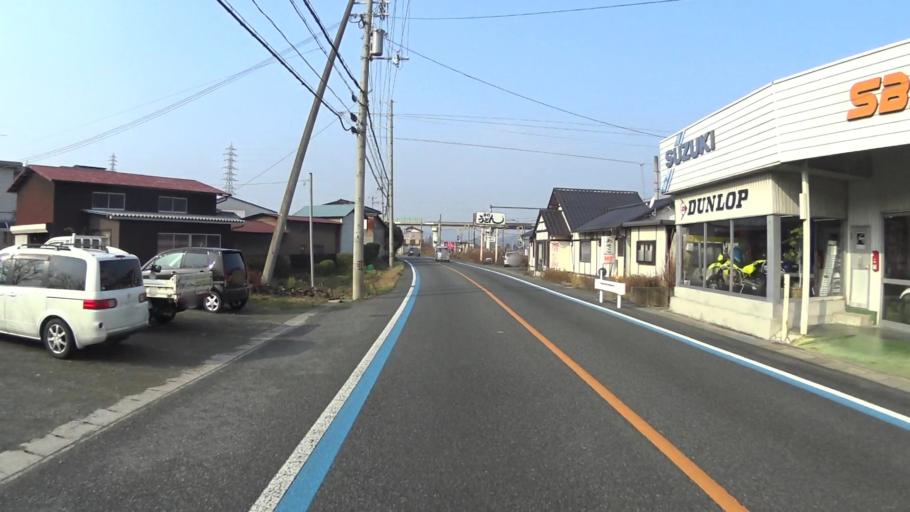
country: JP
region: Kyoto
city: Ayabe
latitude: 35.3038
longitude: 135.1935
